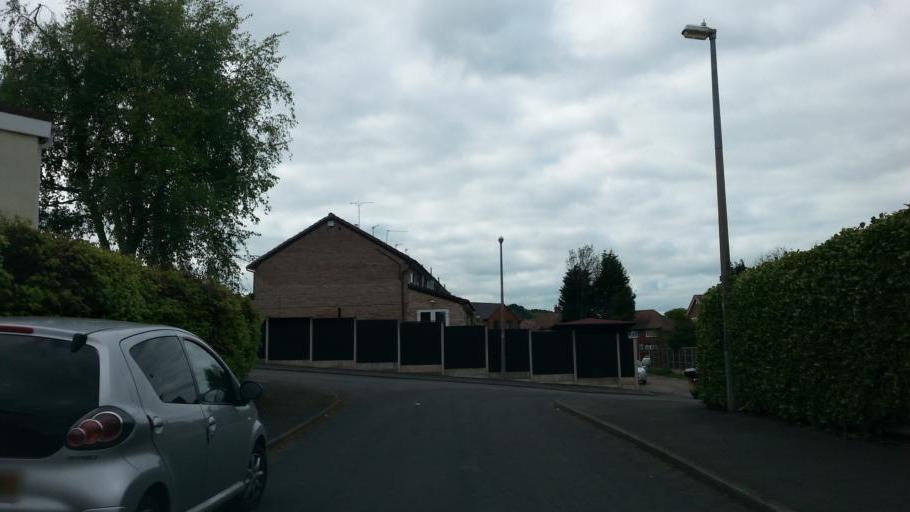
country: GB
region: England
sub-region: Dudley
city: Kingswinford
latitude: 52.4771
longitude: -2.1686
